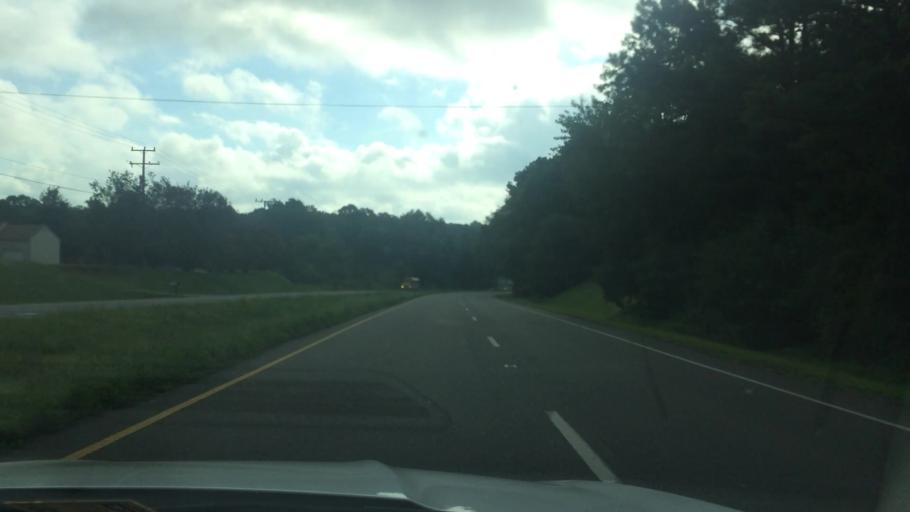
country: US
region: Virginia
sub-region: Gloucester County
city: Gloucester Courthouse
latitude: 37.4260
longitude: -76.5006
